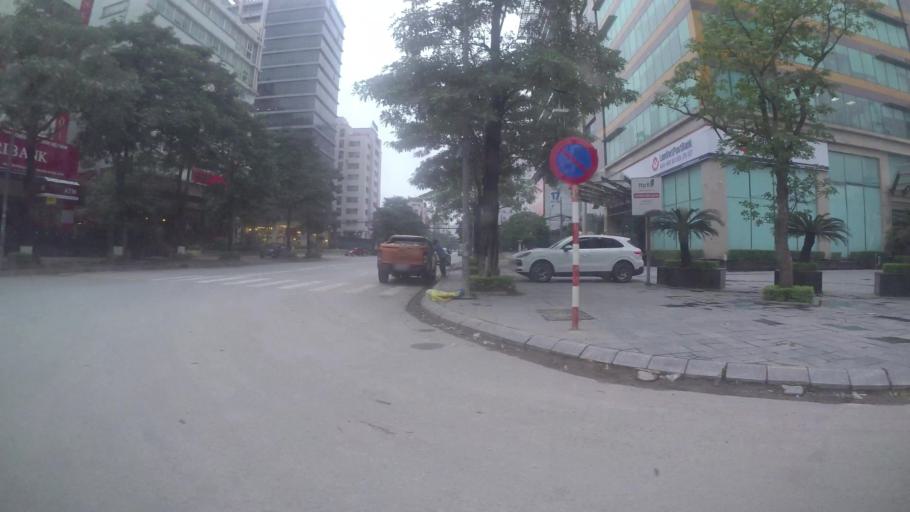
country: VN
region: Ha Noi
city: Cau Dien
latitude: 21.0310
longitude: 105.7819
